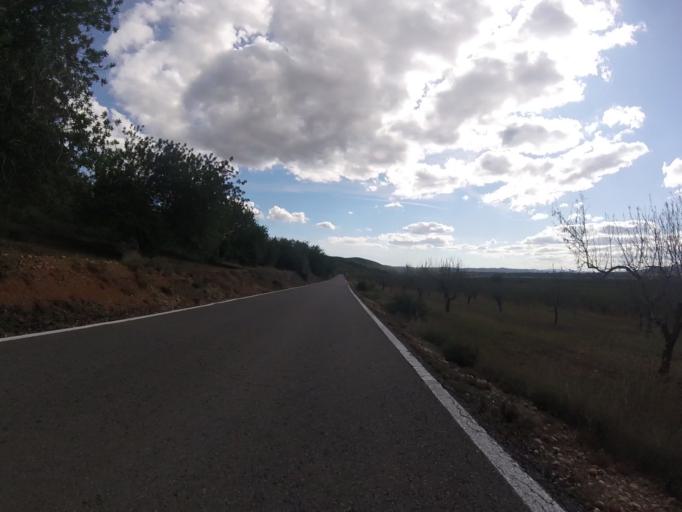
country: ES
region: Valencia
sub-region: Provincia de Castello
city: Cuevas de Vinroma
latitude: 40.3620
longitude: 0.1239
